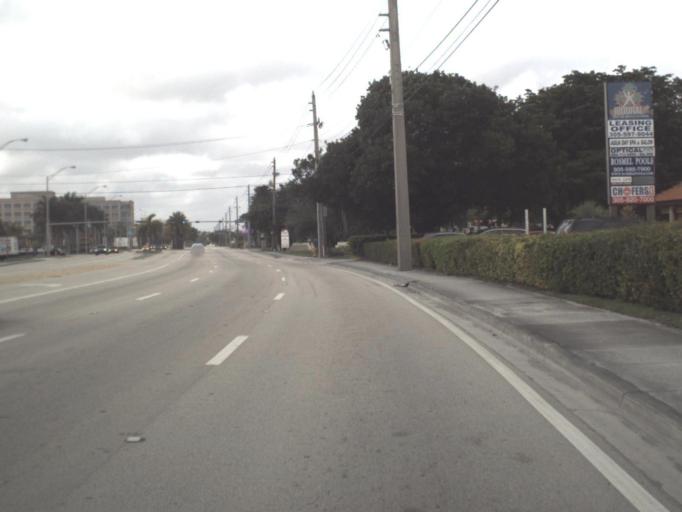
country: US
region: Florida
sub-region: Miami-Dade County
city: Virginia Gardens
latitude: 25.8099
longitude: -80.3275
